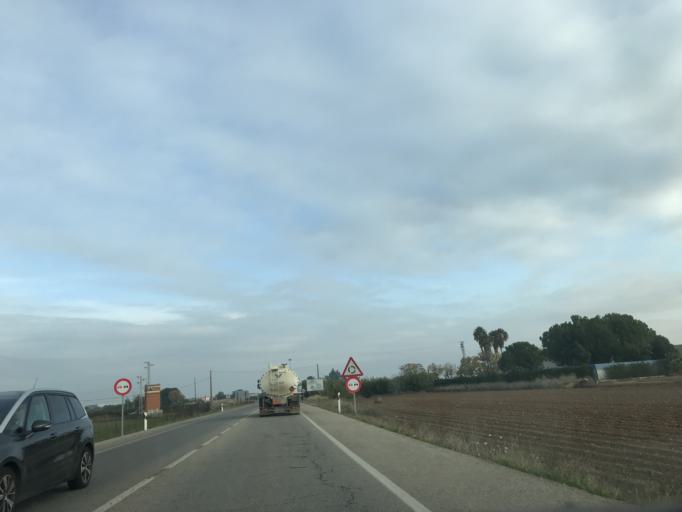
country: ES
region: Andalusia
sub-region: Provincia de Sevilla
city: La Rinconada
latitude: 37.4658
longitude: -5.9721
